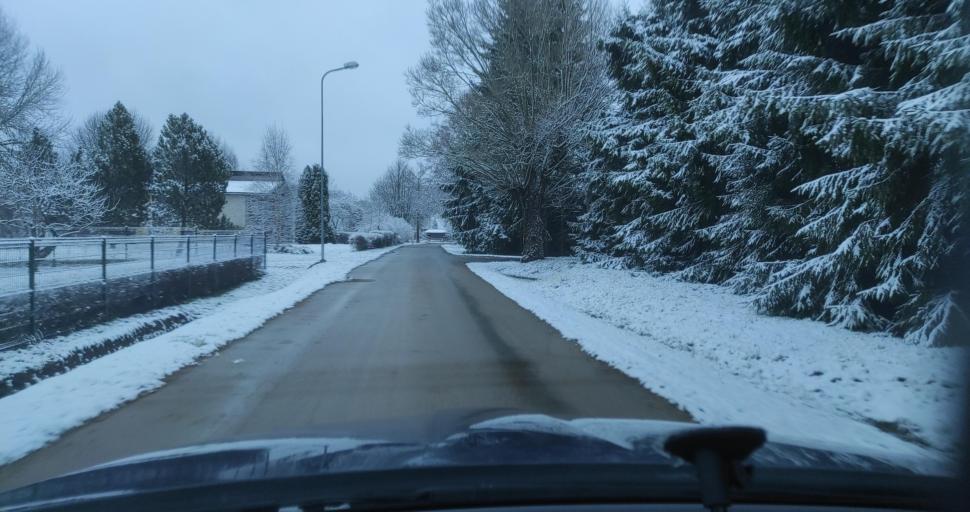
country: LV
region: Skrunda
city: Skrunda
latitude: 56.8759
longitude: 22.2381
